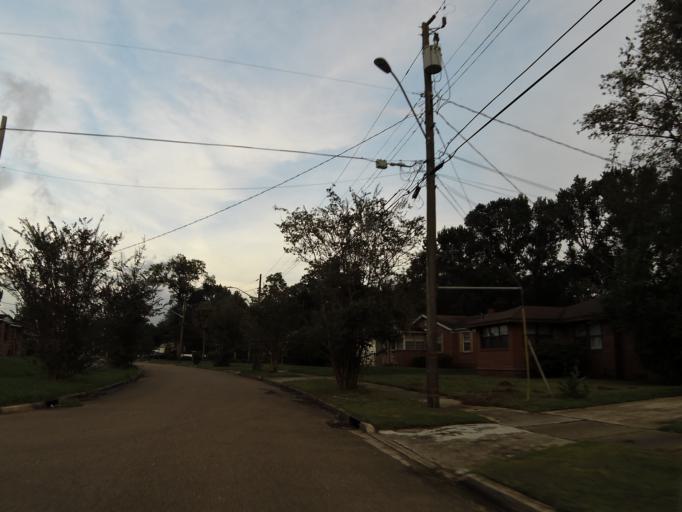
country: US
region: Florida
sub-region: Duval County
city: Jacksonville
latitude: 30.3447
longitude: -81.6944
